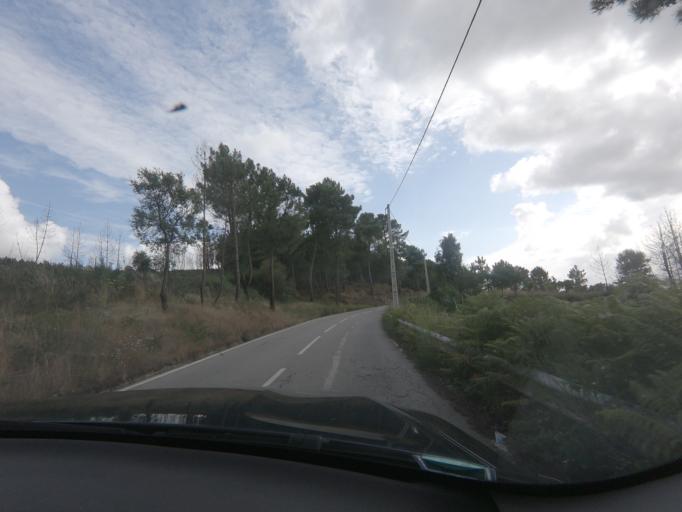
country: PT
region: Vila Real
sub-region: Vila Real
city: Vila Real
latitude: 41.2607
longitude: -7.7112
